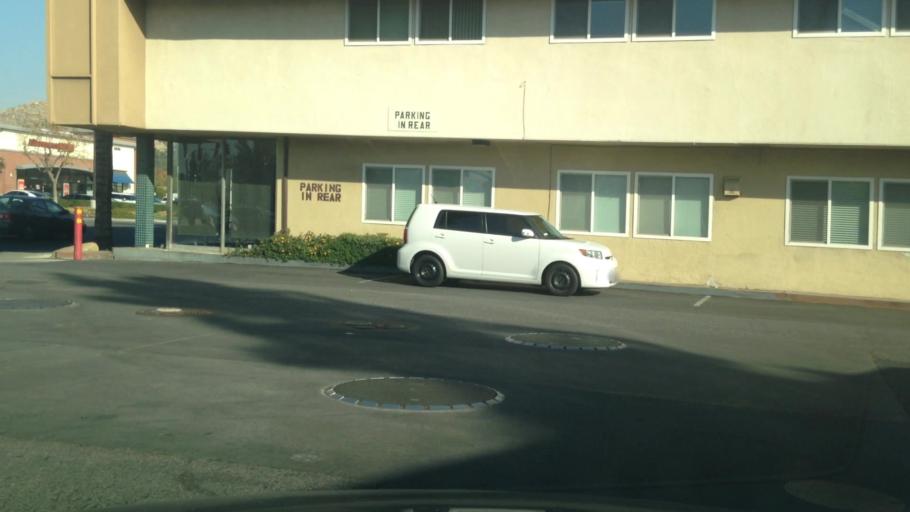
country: US
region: California
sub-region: Riverside County
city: Riverside
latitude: 33.9534
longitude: -117.3903
